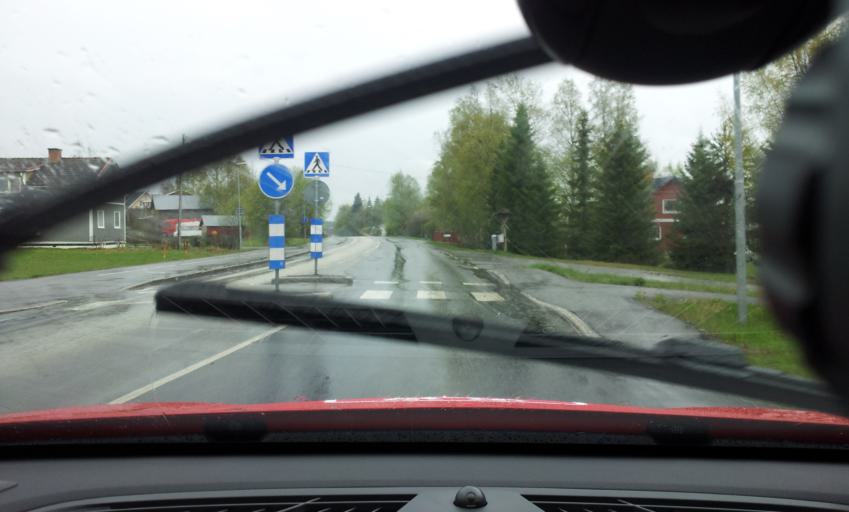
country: SE
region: Jaemtland
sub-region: OEstersunds Kommun
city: Brunflo
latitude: 63.1214
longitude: 14.7817
